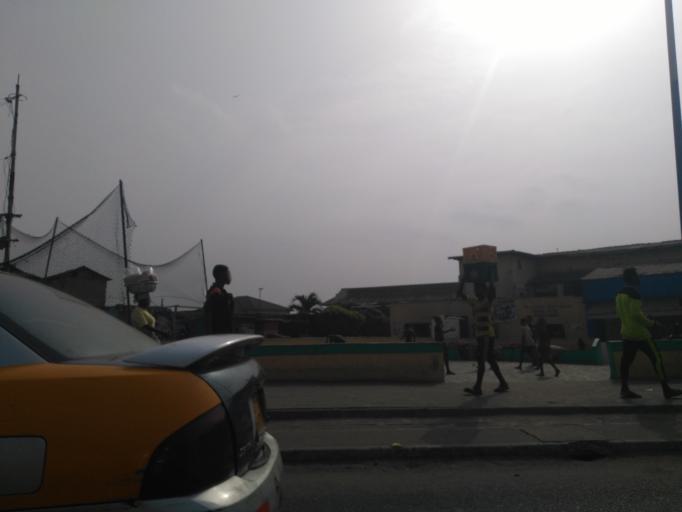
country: GH
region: Greater Accra
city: Accra
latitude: 5.5362
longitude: -0.2108
